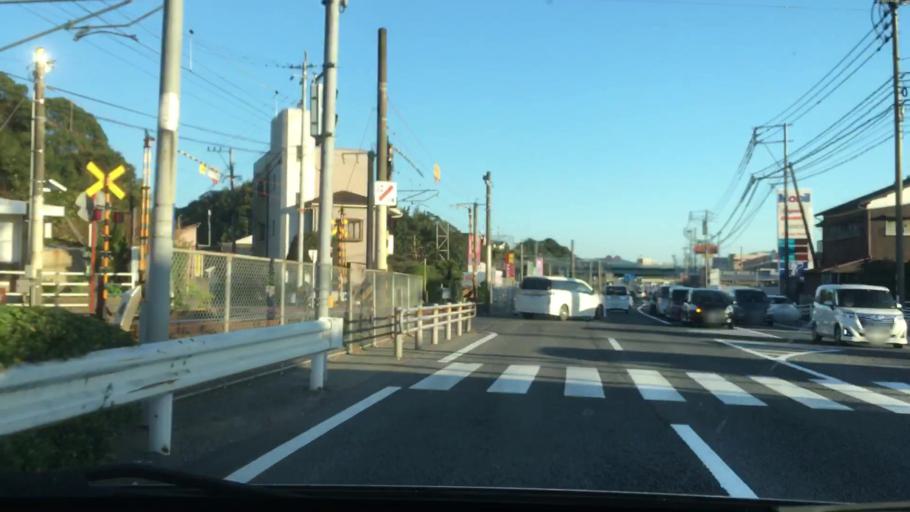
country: JP
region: Nagasaki
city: Sasebo
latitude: 33.1515
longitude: 129.7798
